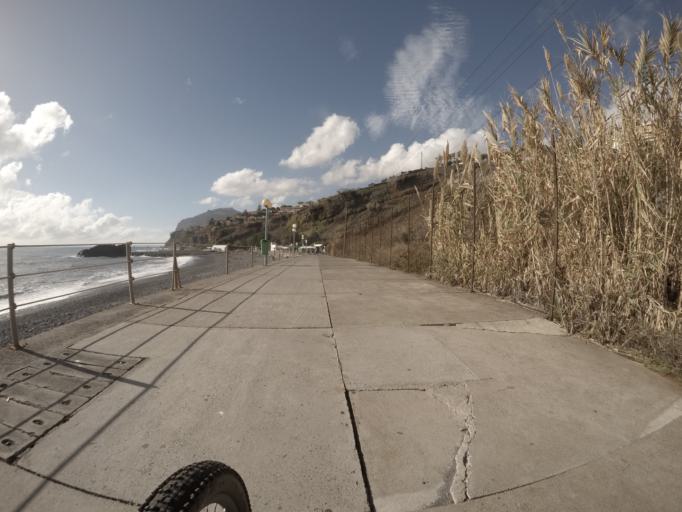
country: PT
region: Madeira
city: Camara de Lobos
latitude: 32.6413
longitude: -16.9536
